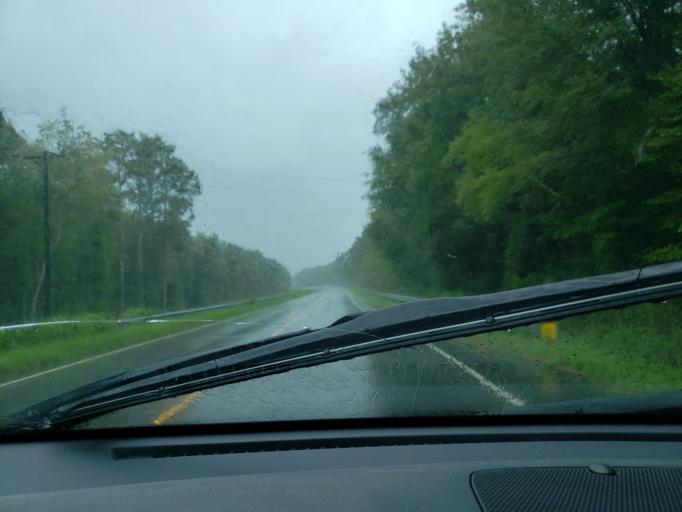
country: US
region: North Carolina
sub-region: Bladen County
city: Elizabethtown
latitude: 34.5254
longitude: -78.6495
